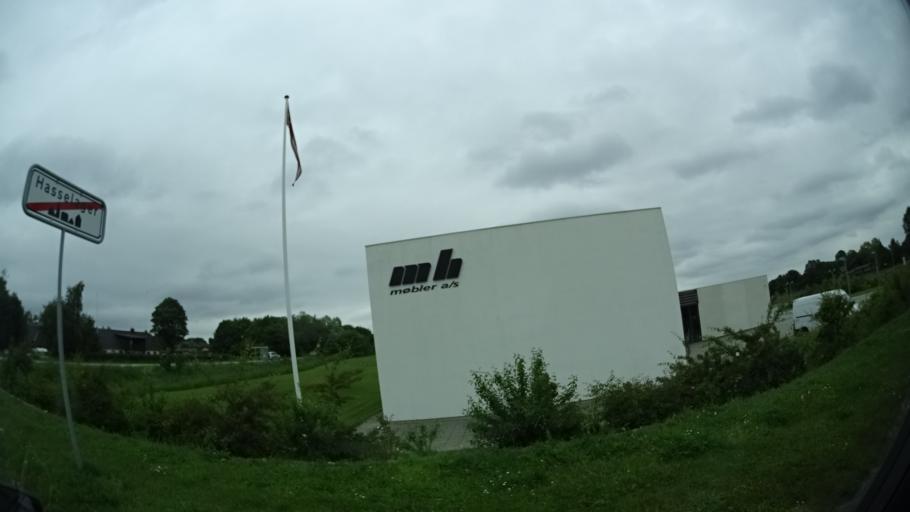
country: DK
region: Central Jutland
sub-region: Arhus Kommune
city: Kolt
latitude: 56.1028
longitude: 10.0789
